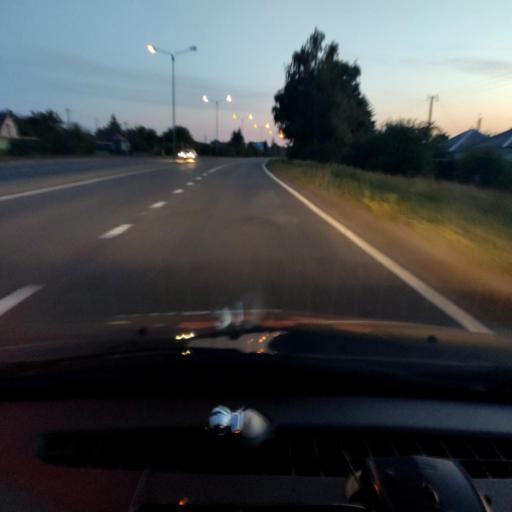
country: RU
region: Belgorod
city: Gubkin
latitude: 51.2720
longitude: 37.5816
